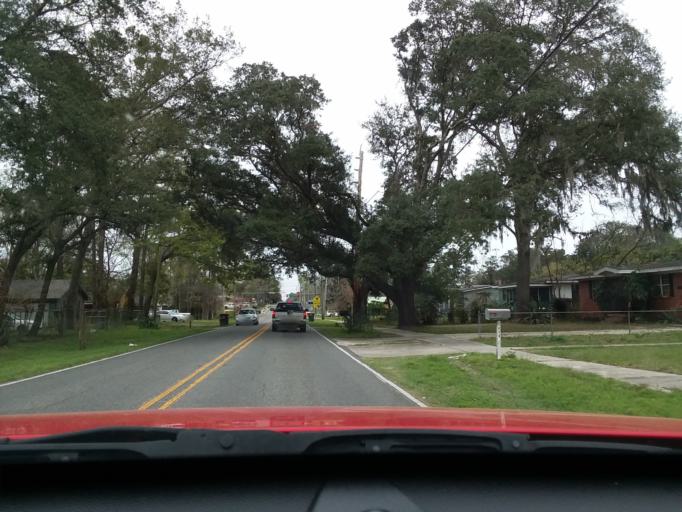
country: US
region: Florida
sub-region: Duval County
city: Jacksonville
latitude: 30.2919
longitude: -81.7407
